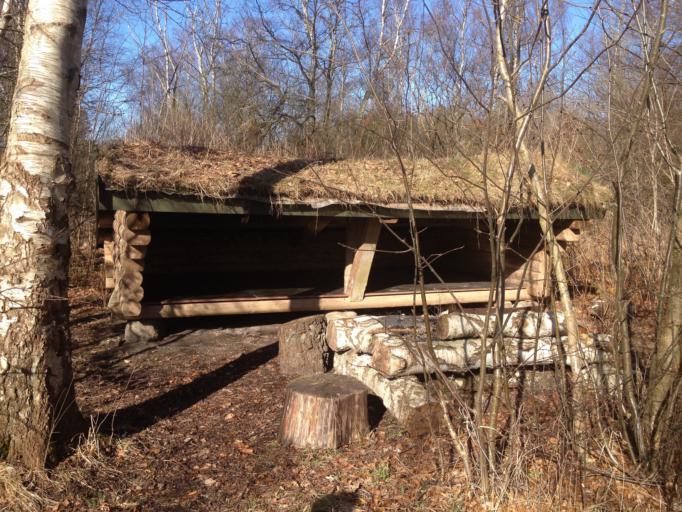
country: DK
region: Capital Region
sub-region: Egedal Kommune
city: Ganlose
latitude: 55.8180
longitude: 12.2591
